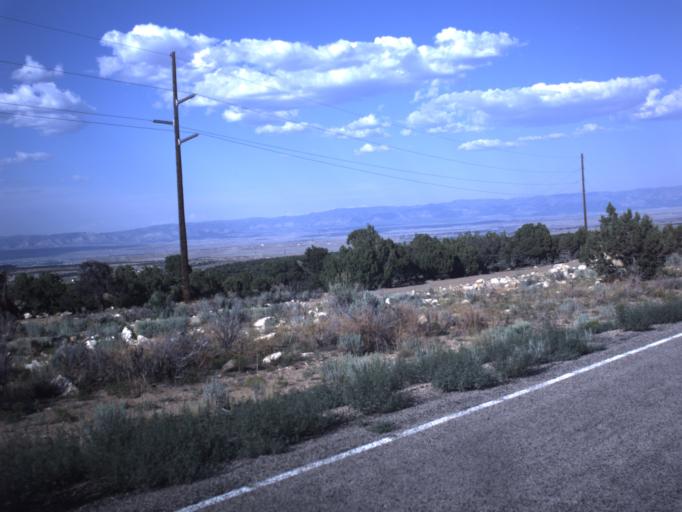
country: US
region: Utah
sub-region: Emery County
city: Huntington
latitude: 39.4869
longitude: -110.9386
